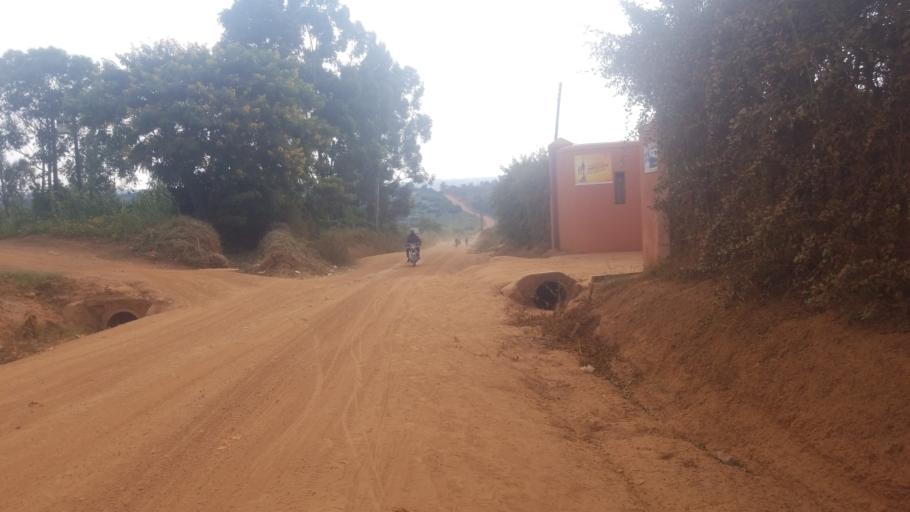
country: UG
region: Central Region
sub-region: Sembabule District
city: Sembabule
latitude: -0.0799
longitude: 31.4572
